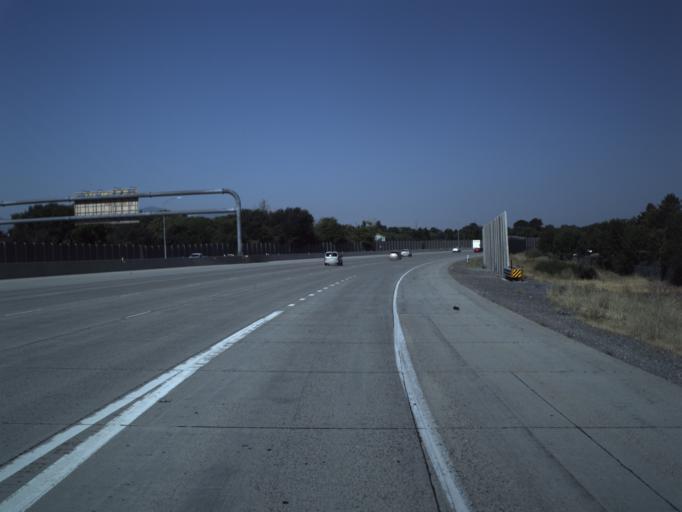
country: US
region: Utah
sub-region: Salt Lake County
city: Taylorsville
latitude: 40.6453
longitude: -111.9442
